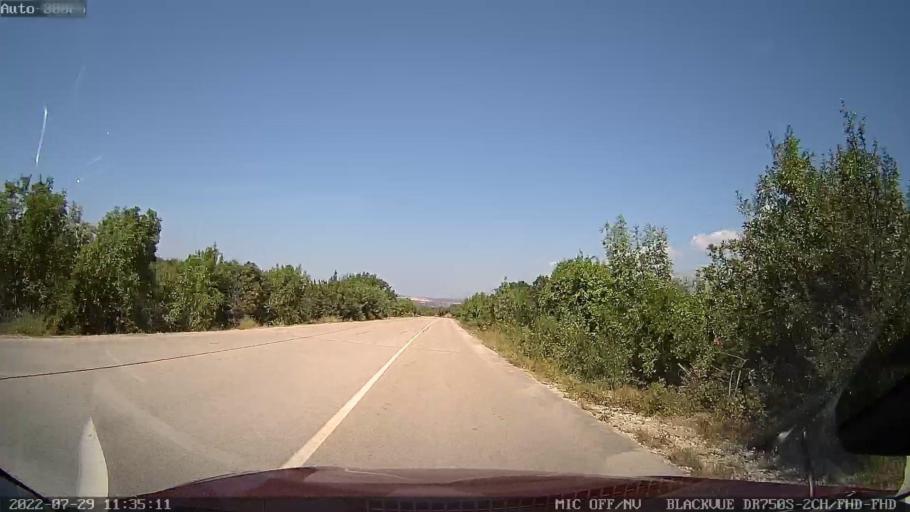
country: HR
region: Zadarska
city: Obrovac
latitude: 44.1811
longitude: 15.7167
